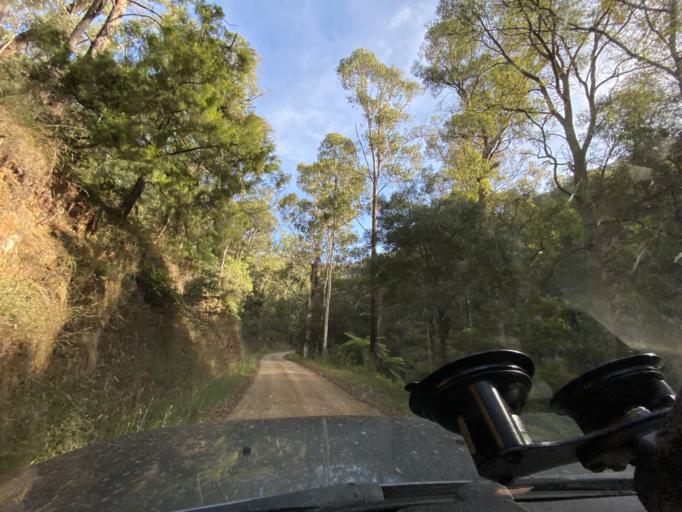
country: AU
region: Victoria
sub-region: Mansfield
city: Mansfield
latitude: -37.5182
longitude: 146.0922
